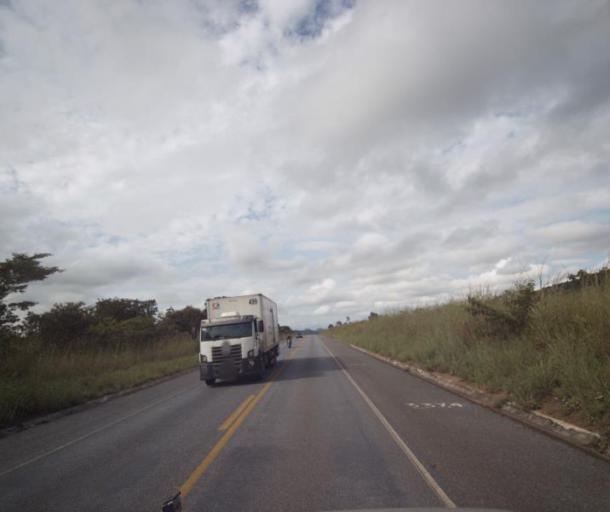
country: BR
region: Goias
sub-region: Pirenopolis
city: Pirenopolis
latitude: -15.5408
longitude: -48.6226
